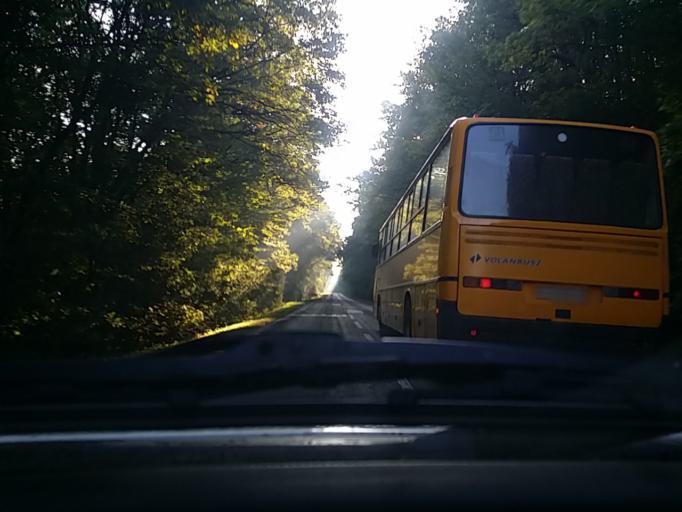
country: HU
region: Pest
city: Visegrad
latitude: 47.7196
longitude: 18.9940
